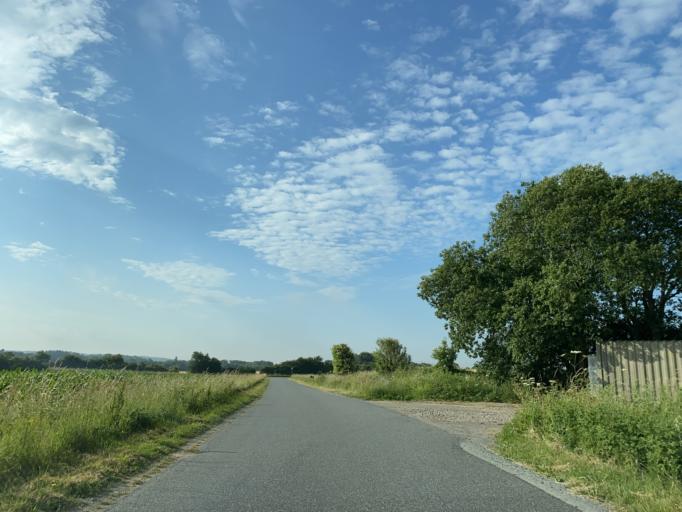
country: DK
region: South Denmark
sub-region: Haderslev Kommune
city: Haderslev
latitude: 55.1896
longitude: 9.4716
